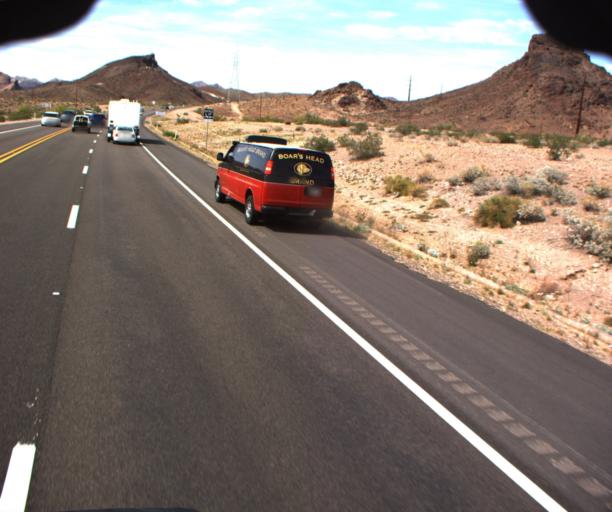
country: US
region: Arizona
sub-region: Mohave County
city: Desert Hills
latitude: 34.5869
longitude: -114.3694
